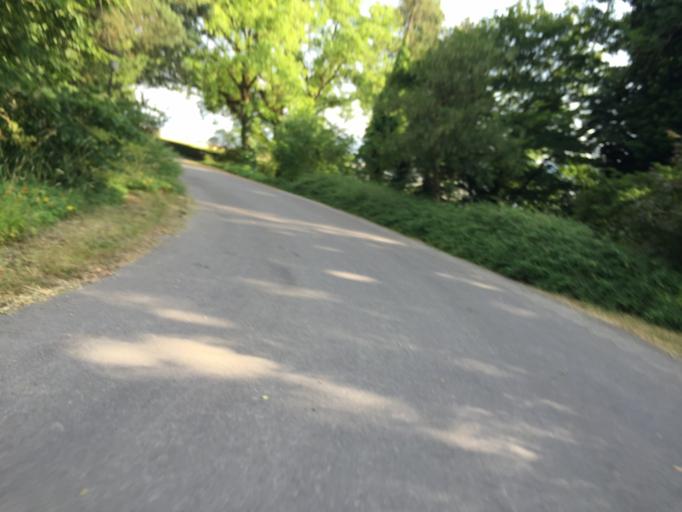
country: CH
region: Bern
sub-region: Bern-Mittelland District
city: Munsingen
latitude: 46.8812
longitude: 7.5495
